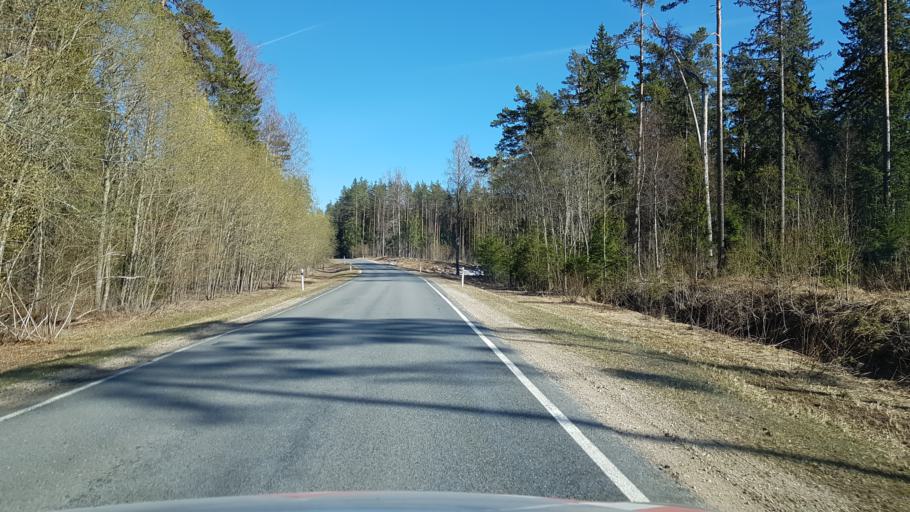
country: EE
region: Laeaene-Virumaa
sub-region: Vinni vald
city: Vinni
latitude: 59.2744
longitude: 26.6183
